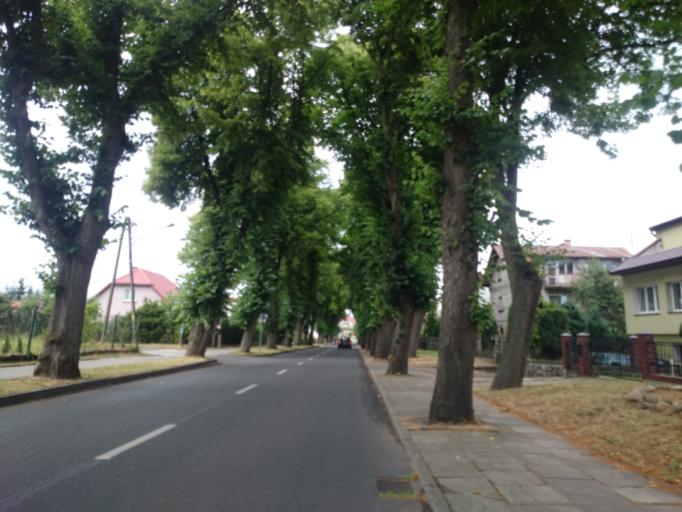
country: PL
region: West Pomeranian Voivodeship
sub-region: Powiat gryfinski
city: Moryn
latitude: 52.8493
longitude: 14.3968
